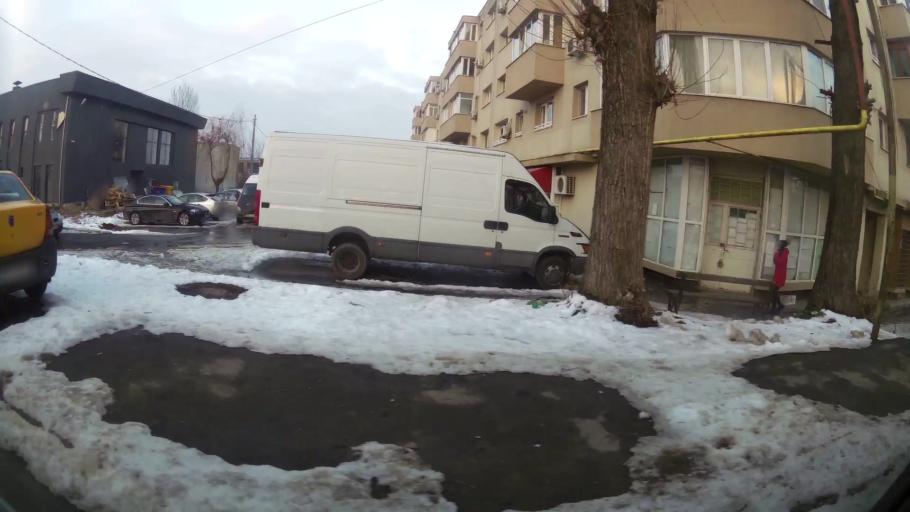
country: RO
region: Ilfov
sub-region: Comuna Popesti-Leordeni
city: Popesti-Leordeni
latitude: 44.3639
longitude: 26.1945
